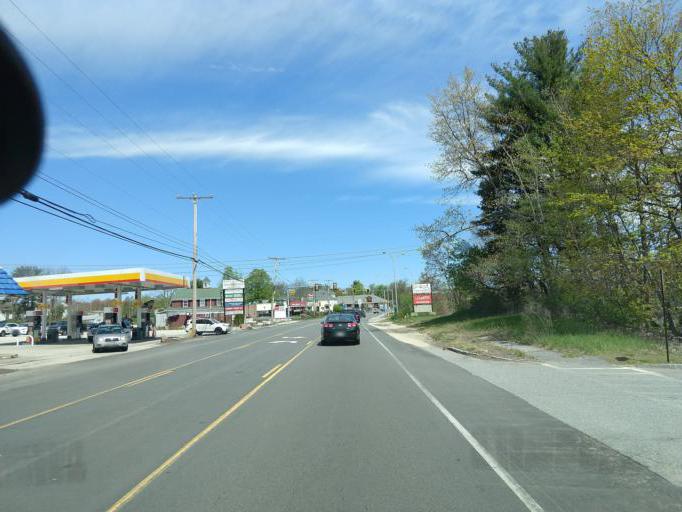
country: US
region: New Hampshire
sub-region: Rockingham County
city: Seabrook
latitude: 42.8977
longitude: -70.8705
